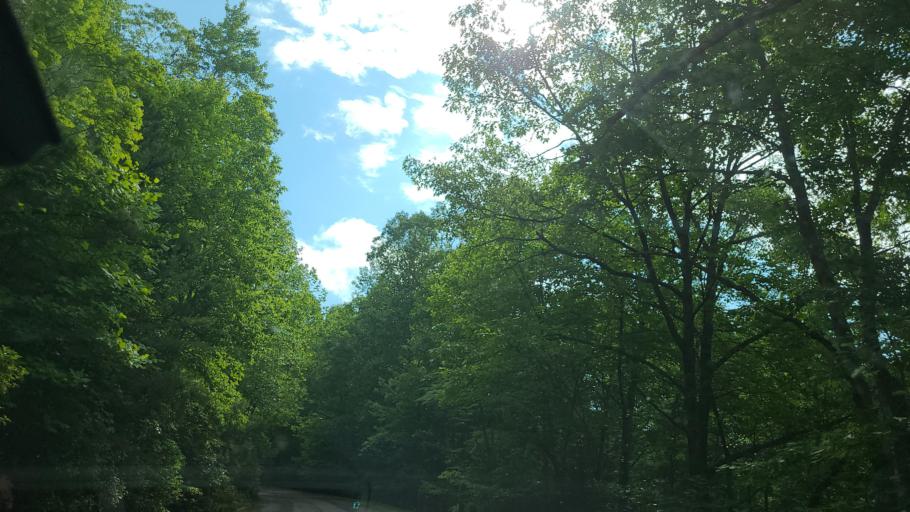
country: US
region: Kentucky
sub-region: Bell County
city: Pineville
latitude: 36.7498
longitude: -83.7182
